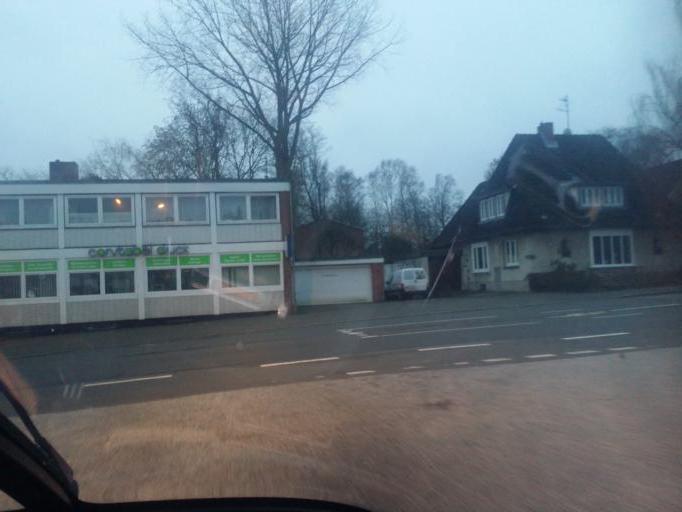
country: DE
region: Schleswig-Holstein
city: Hanerau-Hademarschen
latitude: 54.1278
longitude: 9.4105
